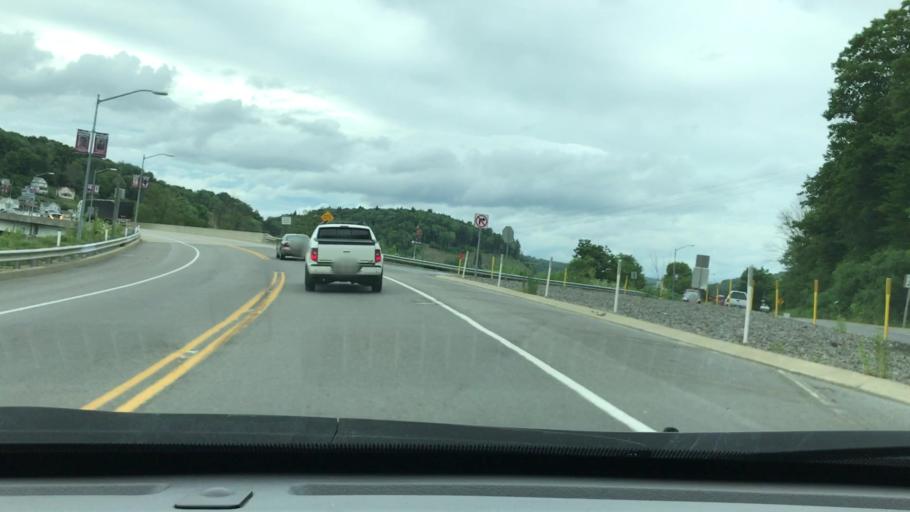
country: US
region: Pennsylvania
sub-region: Elk County
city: Johnsonburg
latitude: 41.4822
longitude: -78.6726
